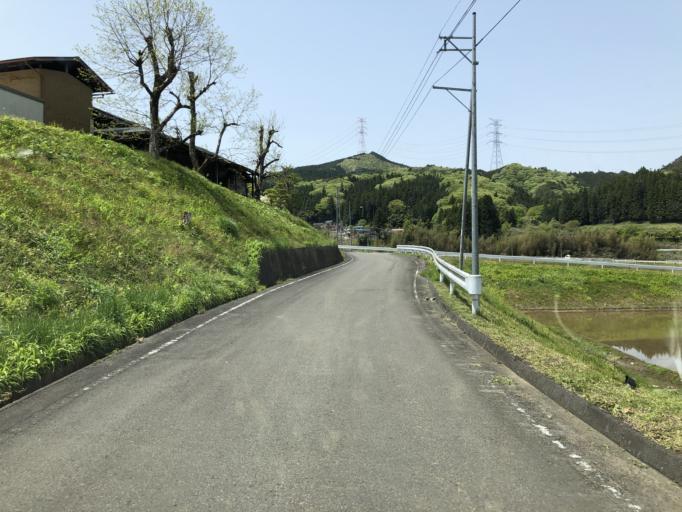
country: JP
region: Fukushima
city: Ishikawa
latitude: 37.0107
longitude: 140.3430
